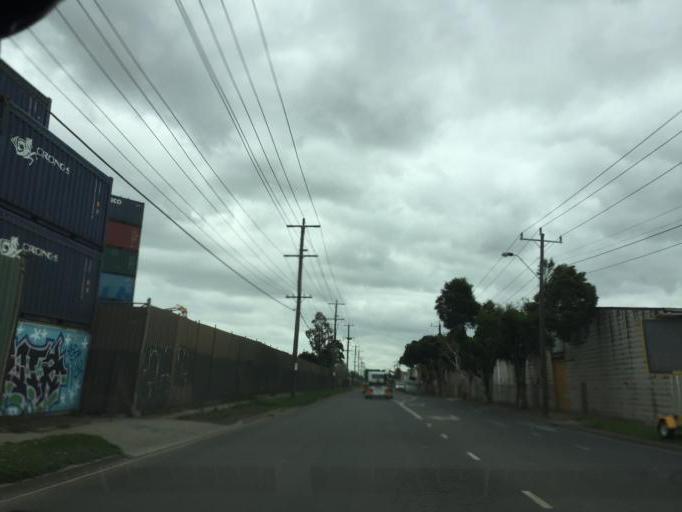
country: AU
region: Victoria
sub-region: Brimbank
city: Brooklyn
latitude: -37.8097
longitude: 144.8560
